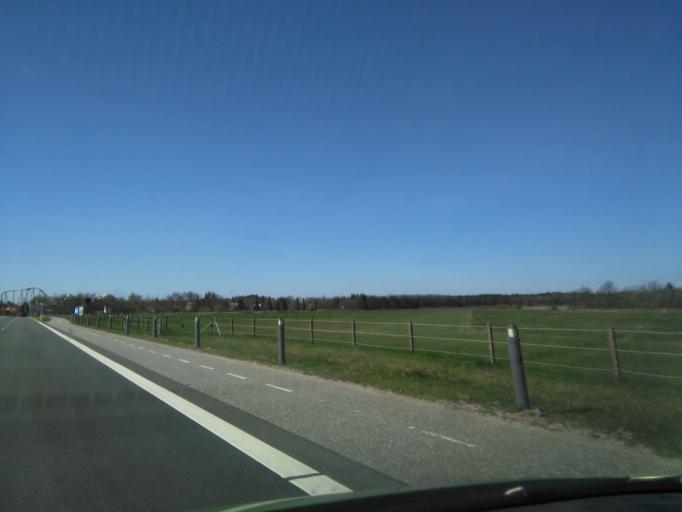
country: DK
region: South Denmark
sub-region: Billund Kommune
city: Billund
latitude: 55.7396
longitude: 9.1269
